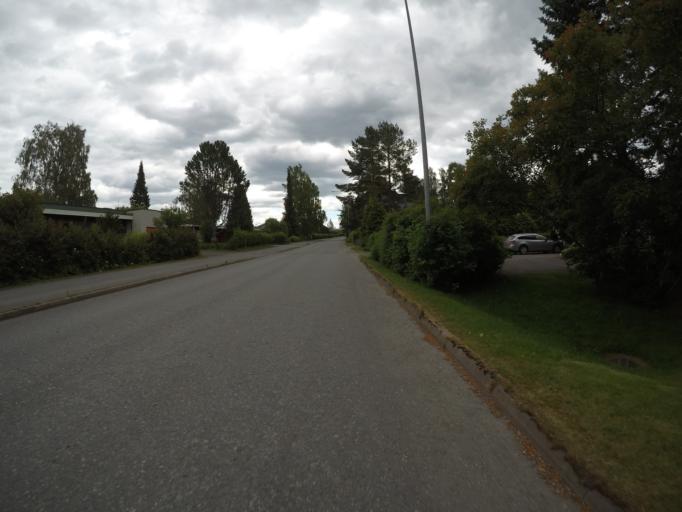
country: FI
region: Haeme
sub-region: Haemeenlinna
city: Haemeenlinna
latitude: 60.9867
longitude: 24.4330
